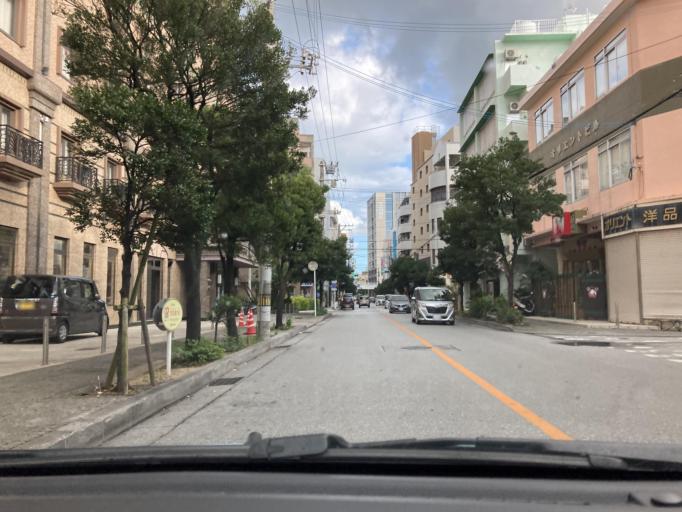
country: JP
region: Okinawa
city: Naha-shi
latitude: 26.2197
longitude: 127.6791
